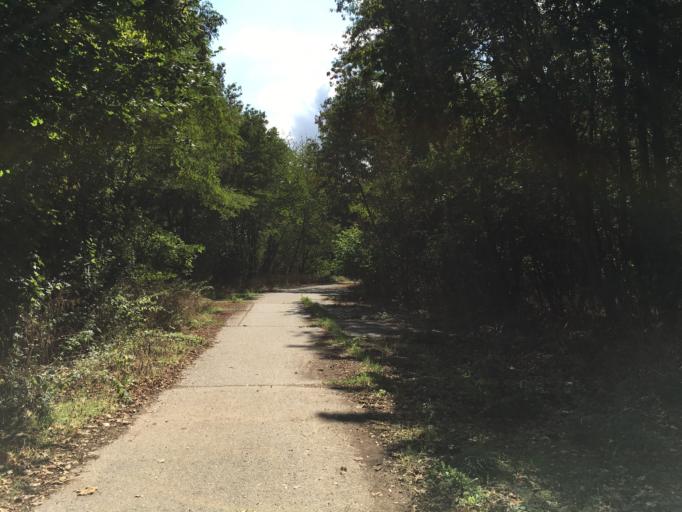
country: DE
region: North Rhine-Westphalia
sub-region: Regierungsbezirk Koln
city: Dueren
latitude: 50.7762
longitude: 6.5078
